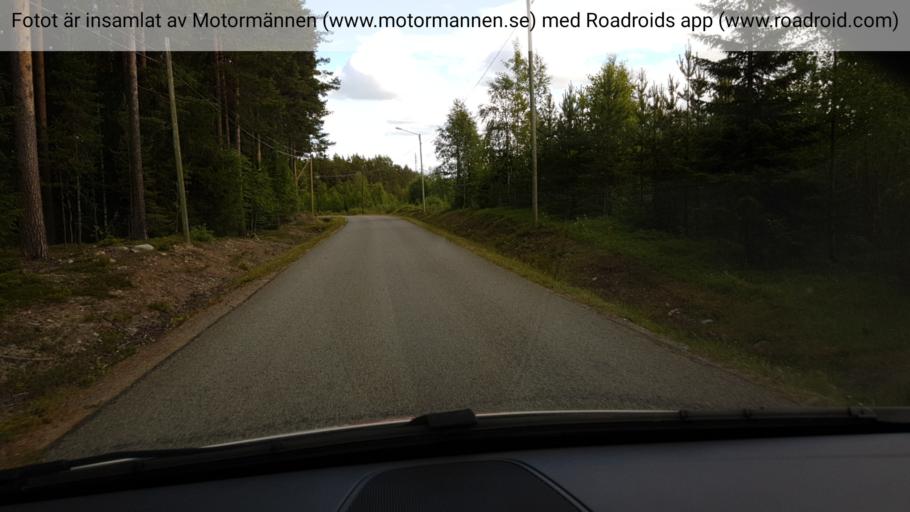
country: SE
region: Vaesterbotten
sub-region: Dorotea Kommun
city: Dorotea
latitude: 64.1064
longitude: 16.3359
